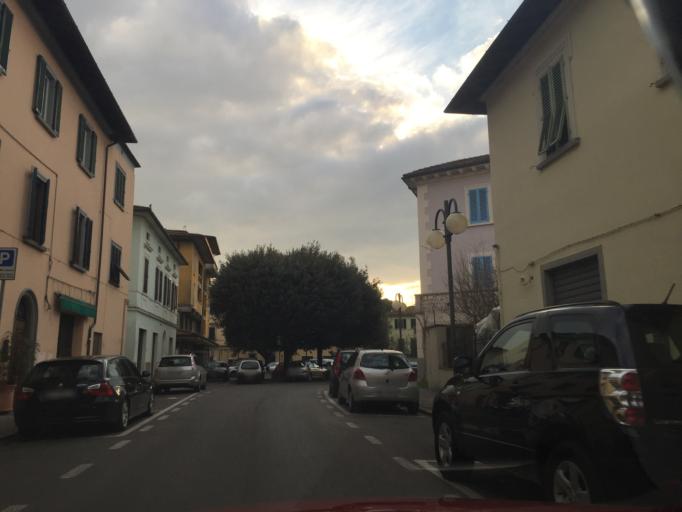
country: IT
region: Tuscany
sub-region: Provincia di Pistoia
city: Borgo a Buggiano
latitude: 43.8782
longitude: 10.7321
